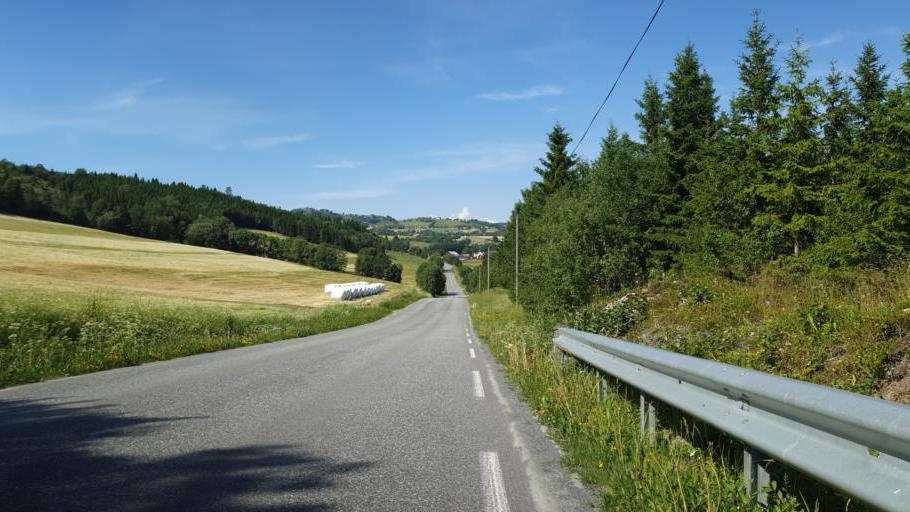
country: NO
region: Nord-Trondelag
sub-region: Leksvik
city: Leksvik
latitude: 63.6575
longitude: 10.6086
